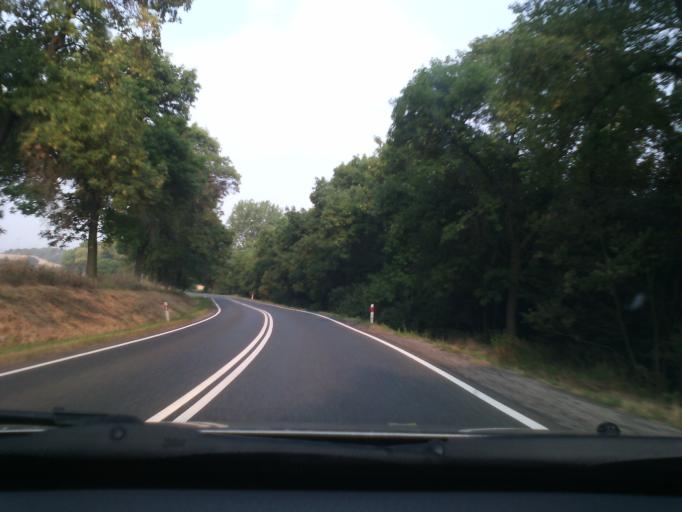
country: PL
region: Lower Silesian Voivodeship
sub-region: Powiat jaworski
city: Bolkow
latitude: 50.9171
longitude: 16.1218
